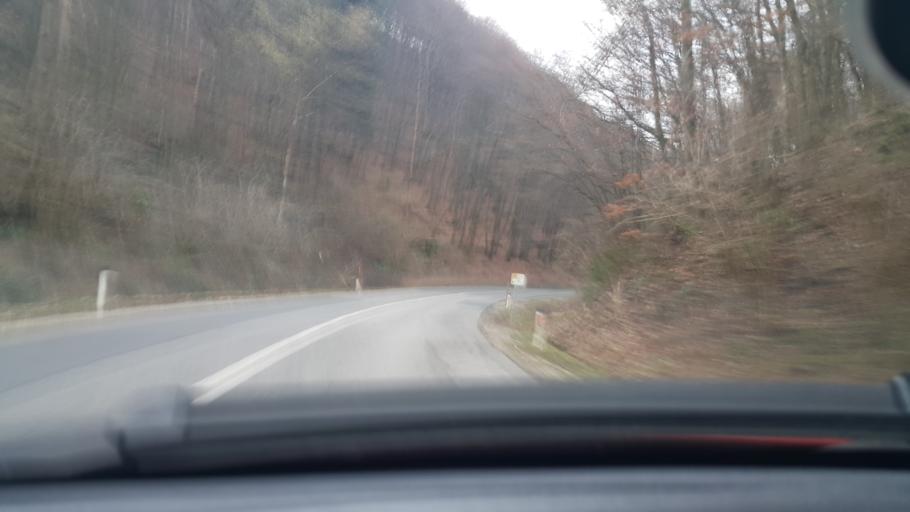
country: SI
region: Bistrica ob Sotli
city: Bistrica ob Sotli
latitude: 46.0358
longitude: 15.6912
